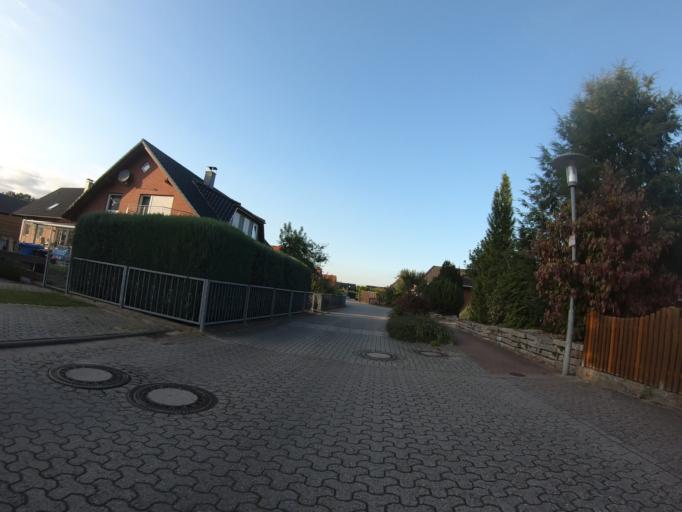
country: DE
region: Lower Saxony
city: Calberlah
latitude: 52.4260
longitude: 10.6124
